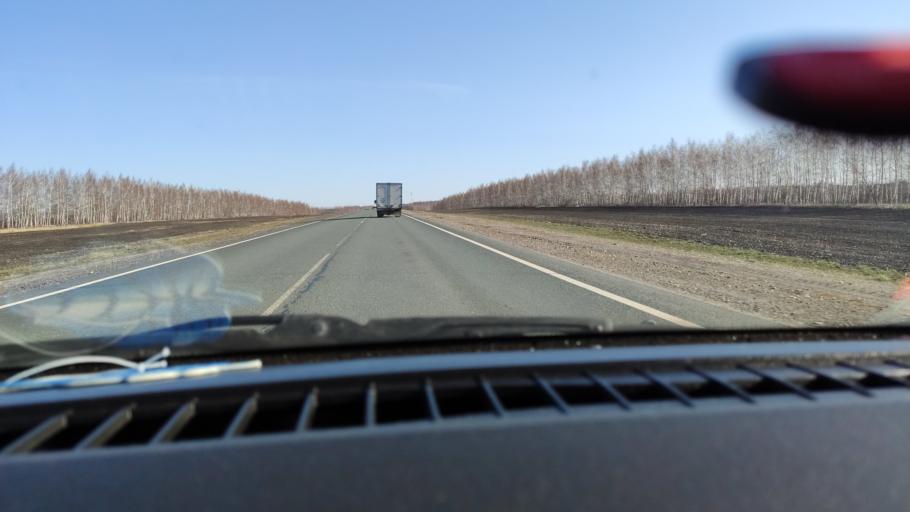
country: RU
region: Samara
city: Syzran'
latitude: 52.9083
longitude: 48.2988
